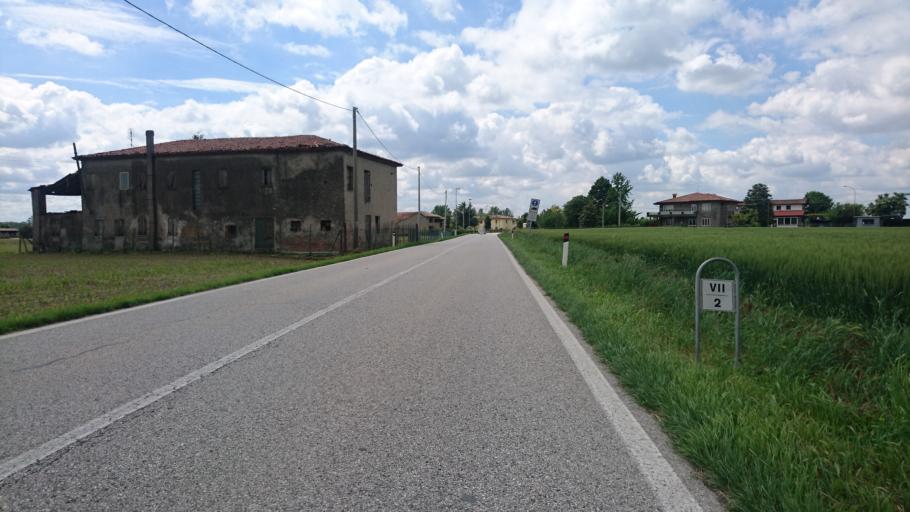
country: IT
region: Veneto
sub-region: Provincia di Padova
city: Villa Estense
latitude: 45.1918
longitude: 11.6833
